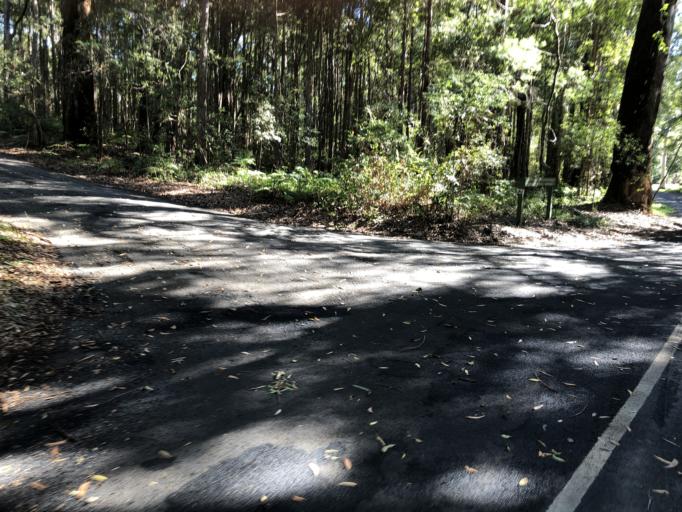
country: AU
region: New South Wales
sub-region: Coffs Harbour
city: Coffs Harbour
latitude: -30.2959
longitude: 153.1248
